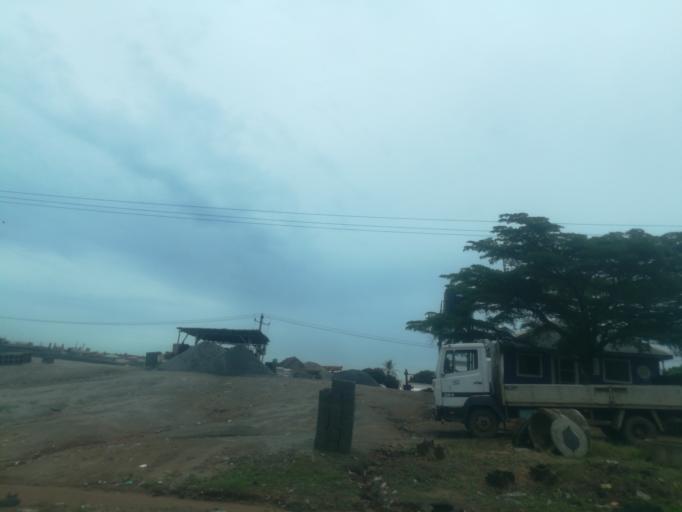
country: NG
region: Oyo
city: Ibadan
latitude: 7.3342
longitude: 3.8877
